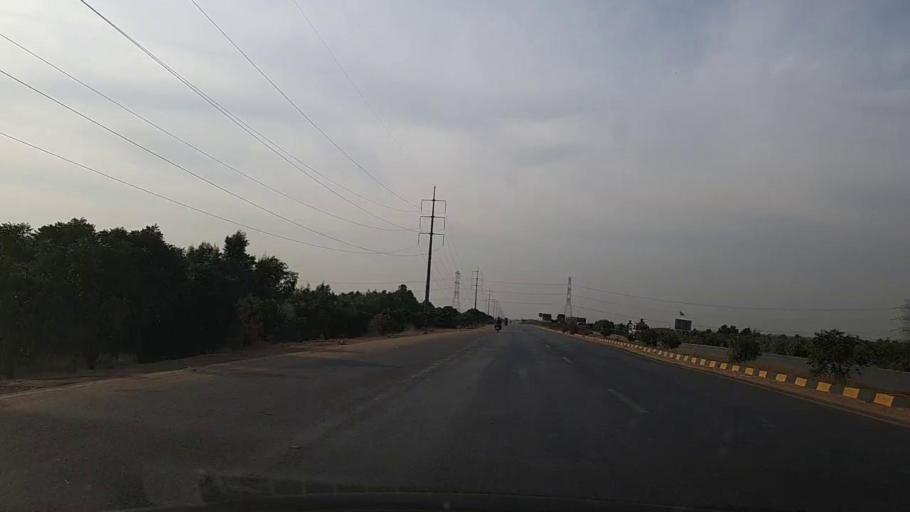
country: PK
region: Sindh
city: Gharo
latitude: 24.8156
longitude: 67.4933
